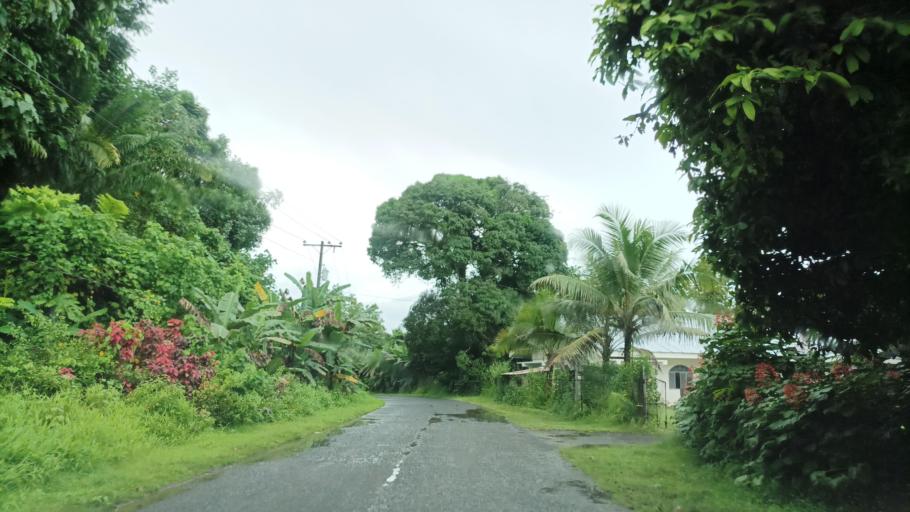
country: FM
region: Pohnpei
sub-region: Sokehs Municipality
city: Palikir - National Government Center
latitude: 6.8295
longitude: 158.1561
